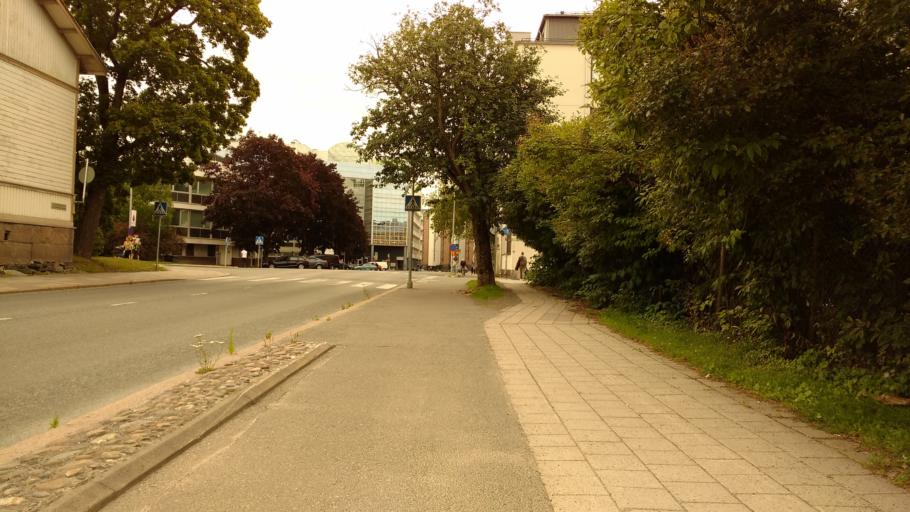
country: FI
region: Varsinais-Suomi
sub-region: Turku
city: Turku
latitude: 60.4507
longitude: 22.2904
